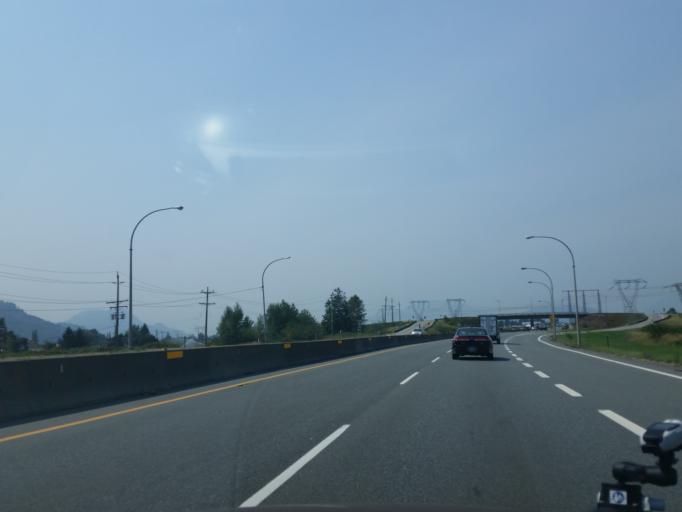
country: CA
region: British Columbia
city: Agassiz
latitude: 49.1550
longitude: -121.8248
